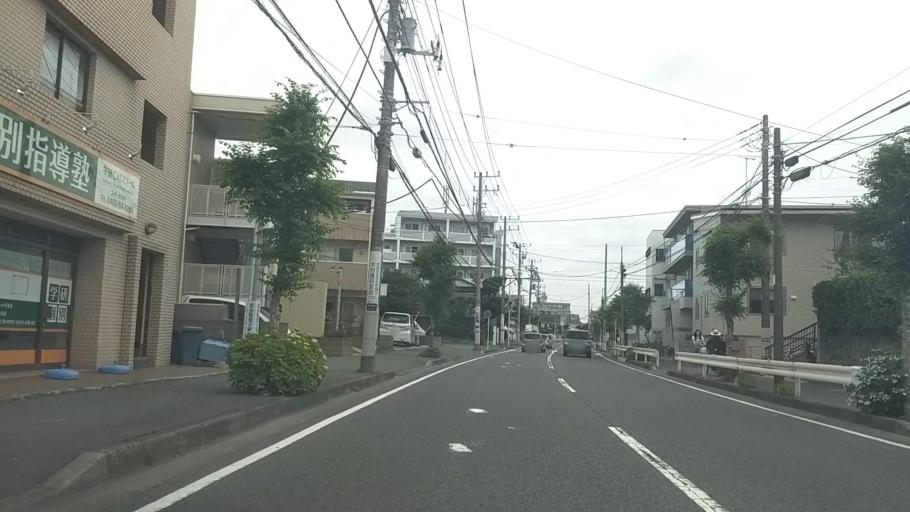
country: JP
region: Kanagawa
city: Fujisawa
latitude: 35.3247
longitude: 139.4663
